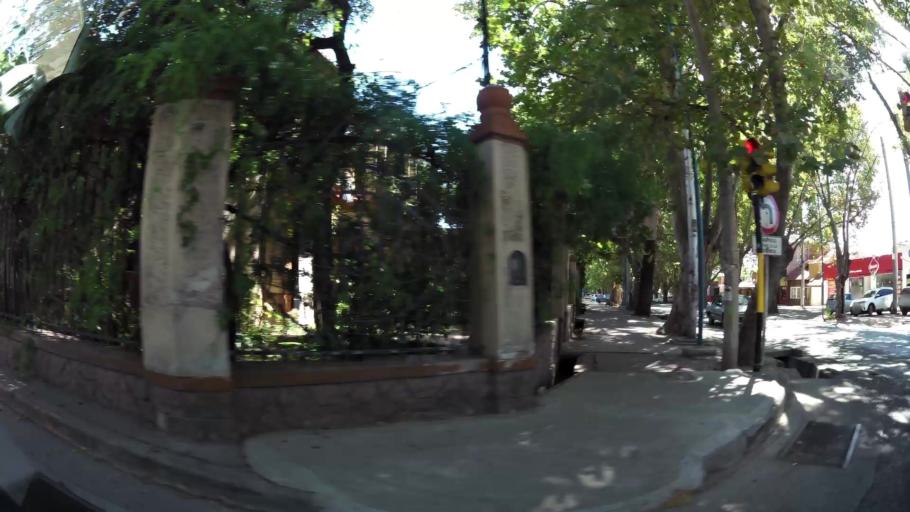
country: AR
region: Mendoza
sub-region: Departamento de Godoy Cruz
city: Godoy Cruz
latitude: -32.9477
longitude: -68.8432
